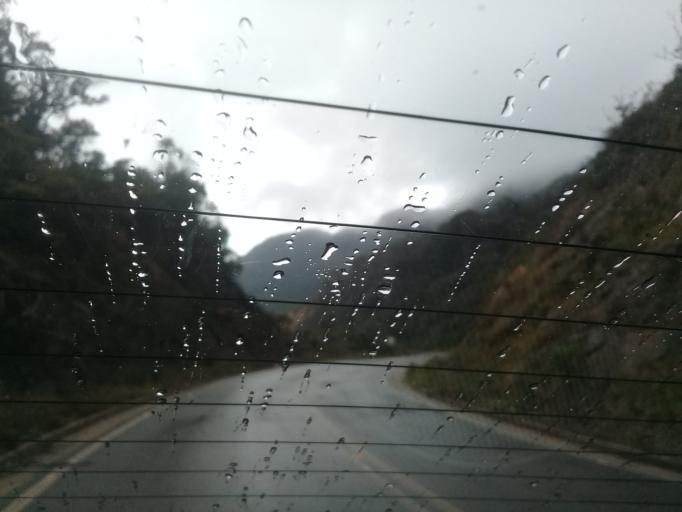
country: CO
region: Cundinamarca
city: Guatavita
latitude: 4.8573
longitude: -73.7608
